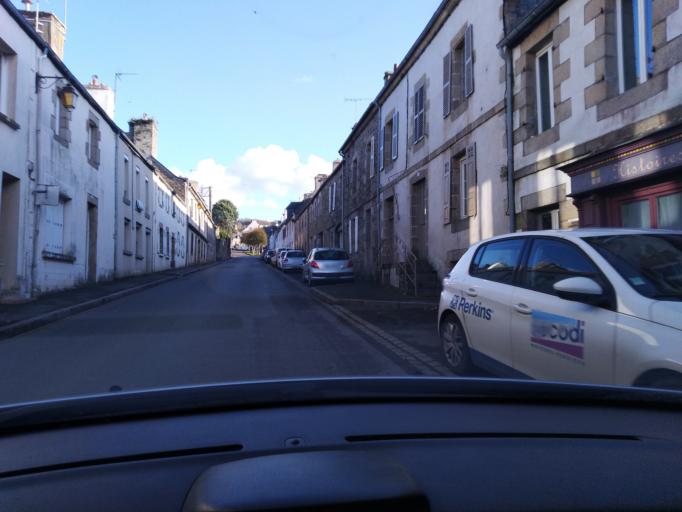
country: FR
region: Brittany
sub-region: Departement des Cotes-d'Armor
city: Plestin-les-Greves
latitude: 48.6541
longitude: -3.6302
